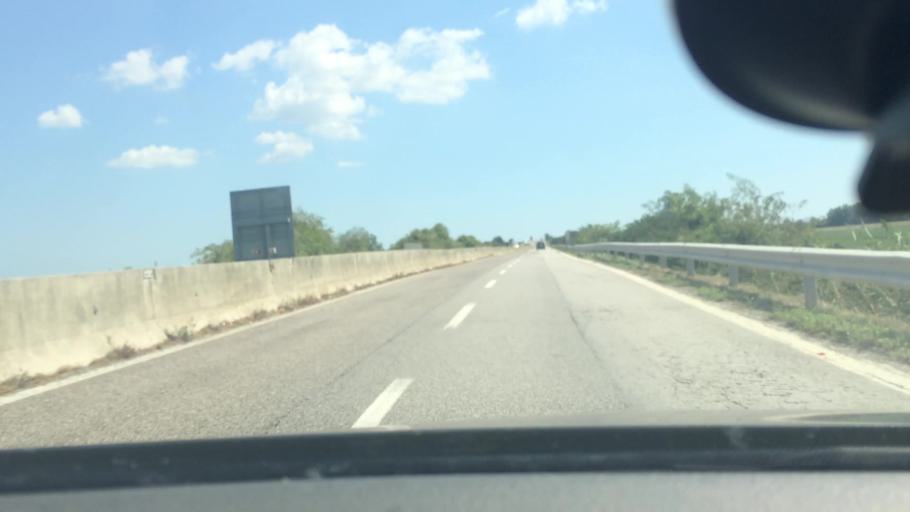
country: IT
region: Emilia-Romagna
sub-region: Provincia di Ferrara
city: Ostellato
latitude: 44.7555
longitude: 11.9444
